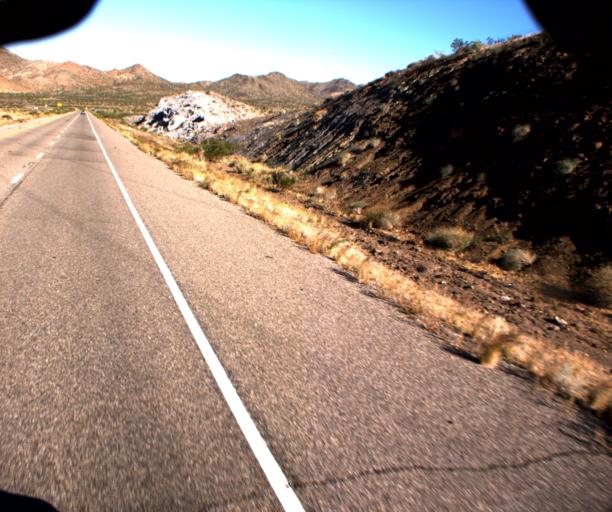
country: US
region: Nevada
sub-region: Clark County
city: Laughlin
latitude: 35.1970
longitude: -114.4153
